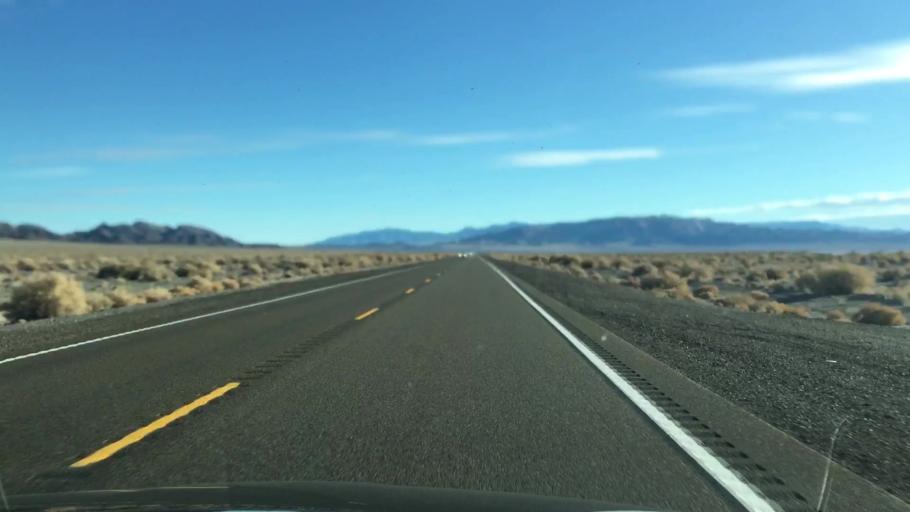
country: US
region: Nevada
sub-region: Nye County
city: Tonopah
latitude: 38.1125
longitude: -117.9294
